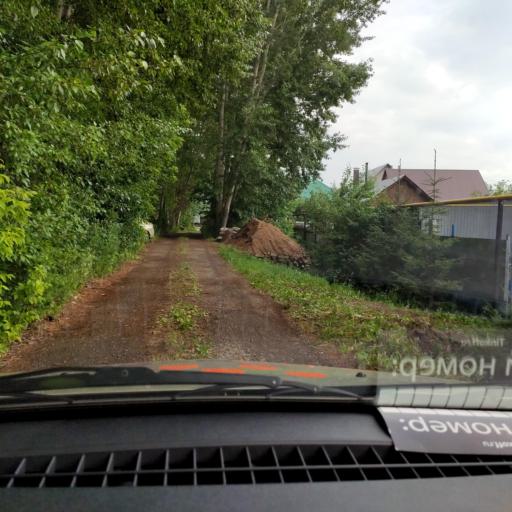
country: RU
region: Bashkortostan
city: Mikhaylovka
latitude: 54.7884
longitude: 55.8993
